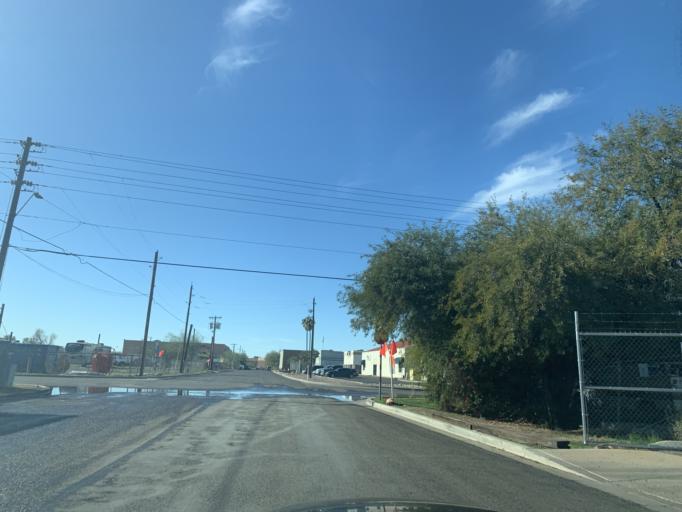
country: US
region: Arizona
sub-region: Maricopa County
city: Tempe Junction
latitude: 33.4183
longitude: -111.9994
